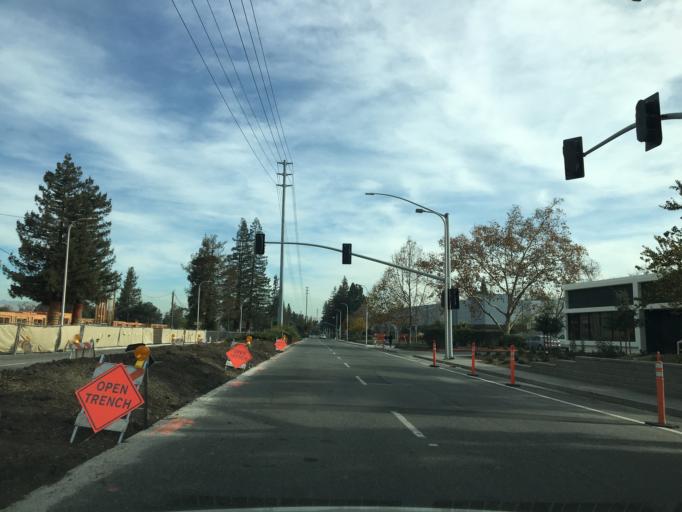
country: US
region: California
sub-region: Santa Clara County
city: Santa Clara
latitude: 37.3800
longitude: -121.9735
